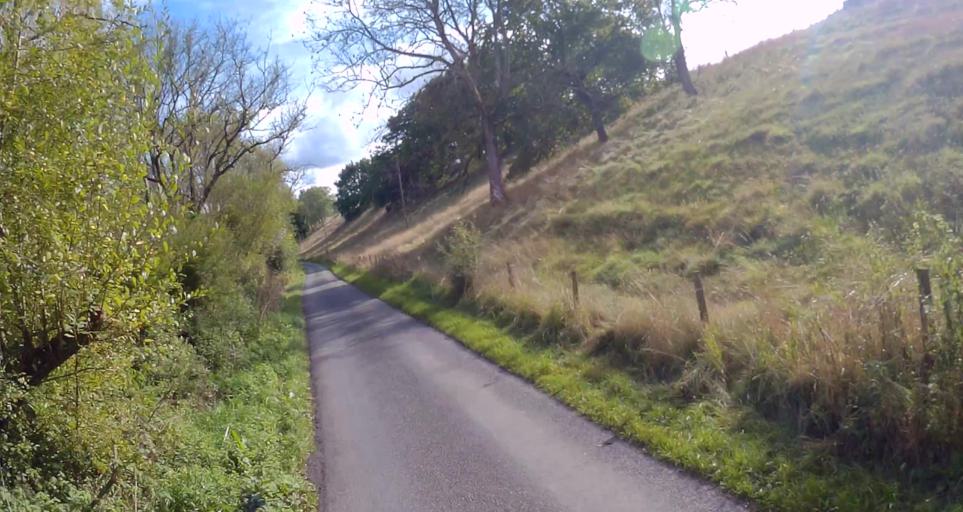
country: GB
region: England
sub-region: Hampshire
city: Kings Worthy
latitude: 51.0893
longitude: -1.2220
